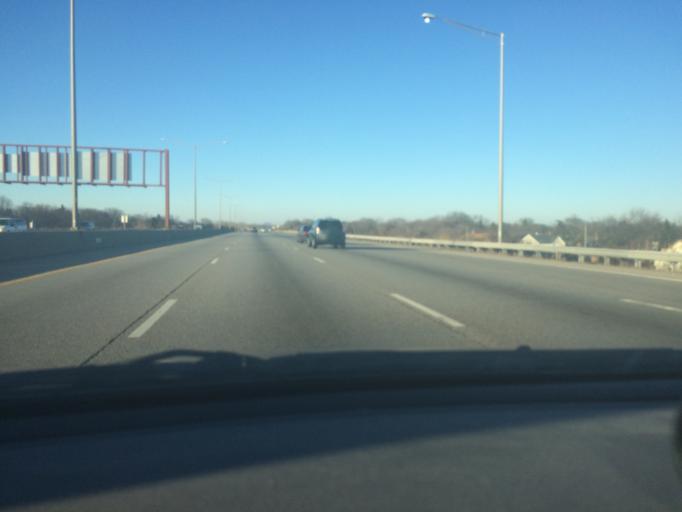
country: US
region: Illinois
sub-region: Cook County
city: Rolling Meadows
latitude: 42.1133
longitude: -88.0030
